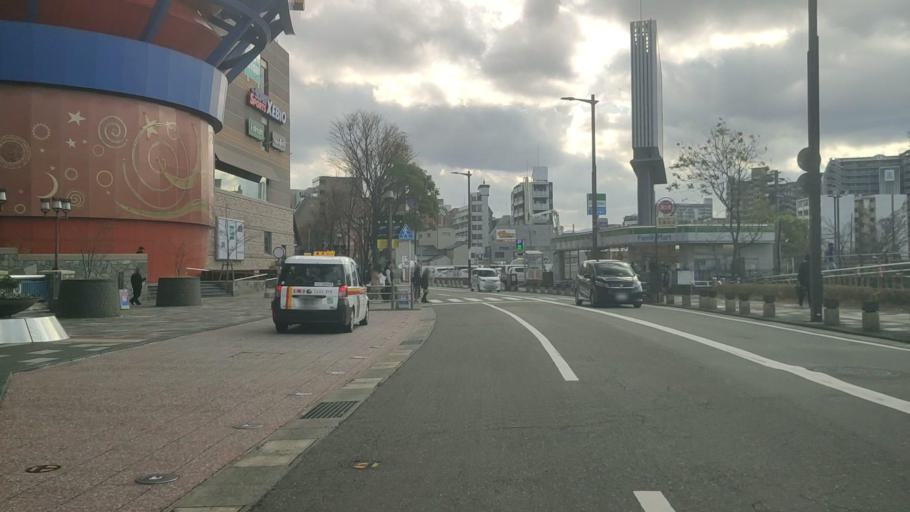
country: JP
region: Fukuoka
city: Fukuoka-shi
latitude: 33.5895
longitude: 130.4101
